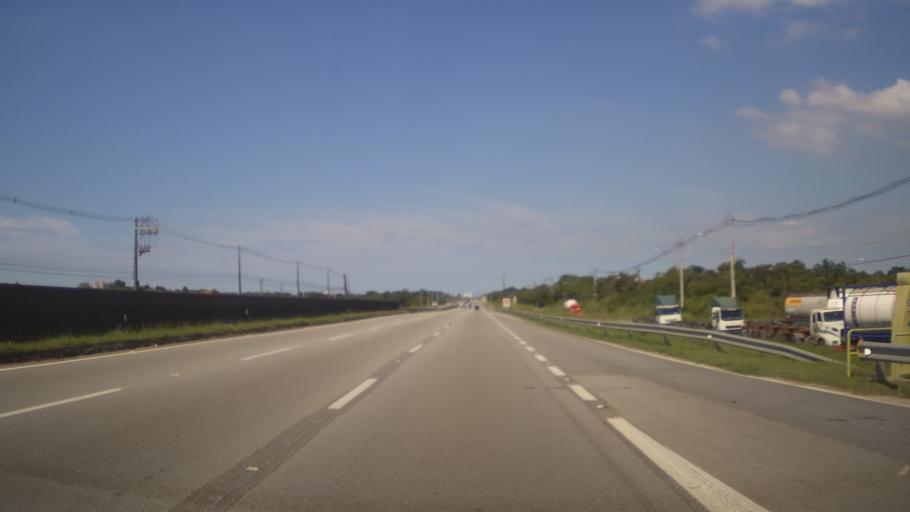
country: BR
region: Sao Paulo
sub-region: Praia Grande
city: Praia Grande
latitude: -23.9931
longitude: -46.4956
